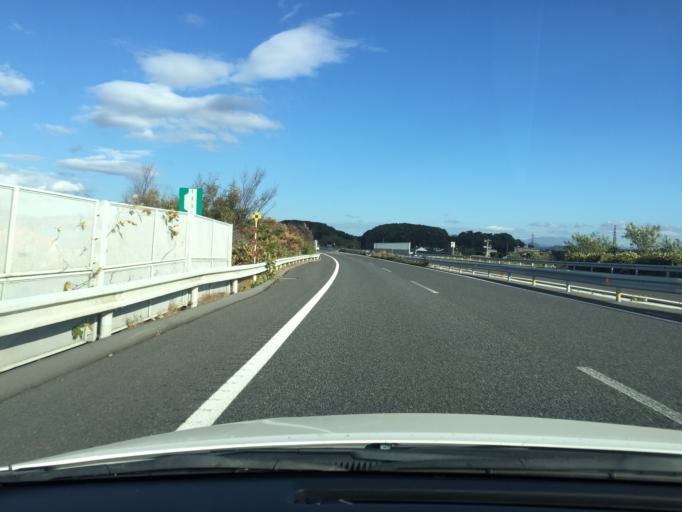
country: JP
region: Fukushima
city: Motomiya
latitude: 37.4596
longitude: 140.3791
